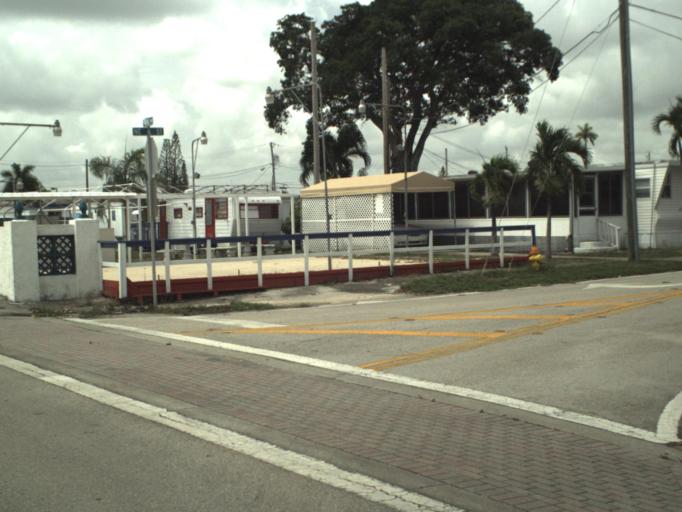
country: US
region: Florida
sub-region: Broward County
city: Hallandale Beach
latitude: 25.9923
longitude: -80.1426
